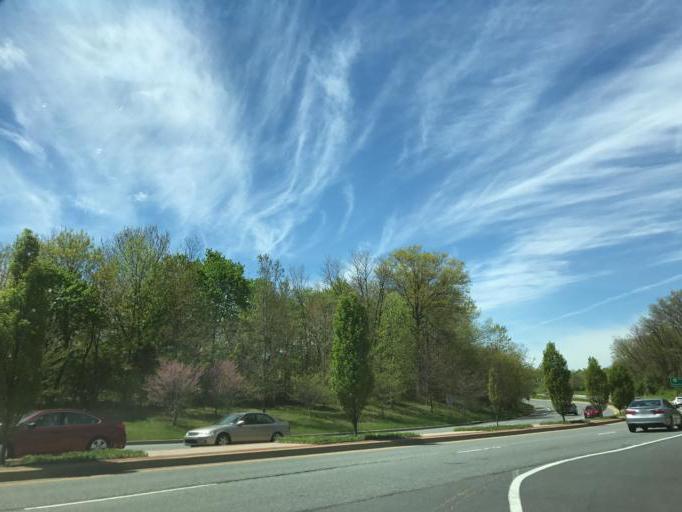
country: US
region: Delaware
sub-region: New Castle County
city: Greenville
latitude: 39.7733
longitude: -75.5876
